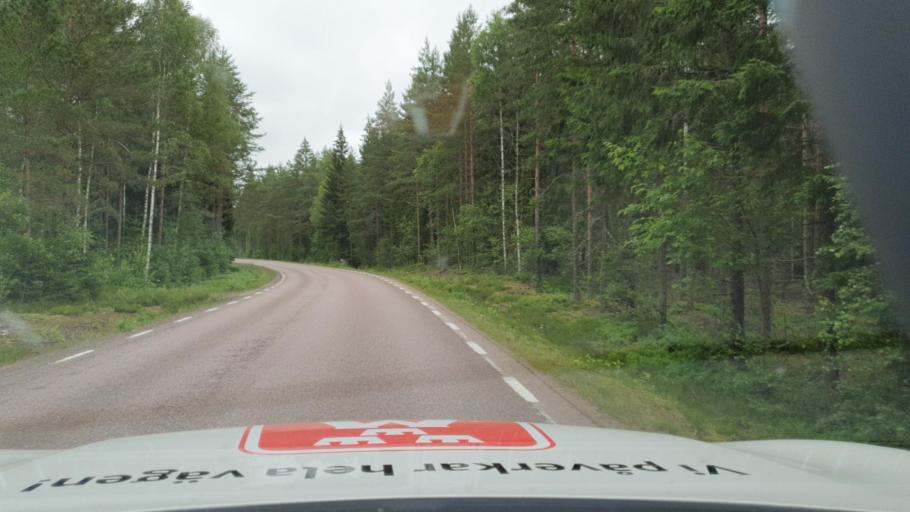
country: SE
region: Vaermland
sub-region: Kristinehamns Kommun
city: Kristinehamn
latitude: 59.4685
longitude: 13.9376
